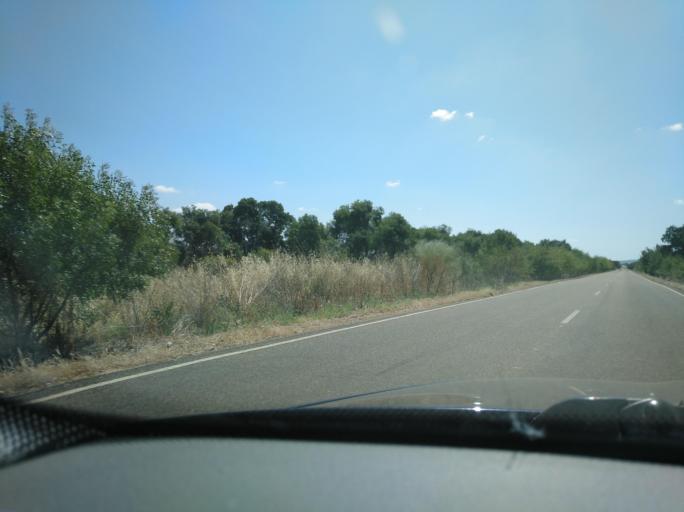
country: ES
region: Extremadura
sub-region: Provincia de Badajoz
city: Olivenza
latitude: 38.7127
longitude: -7.1902
